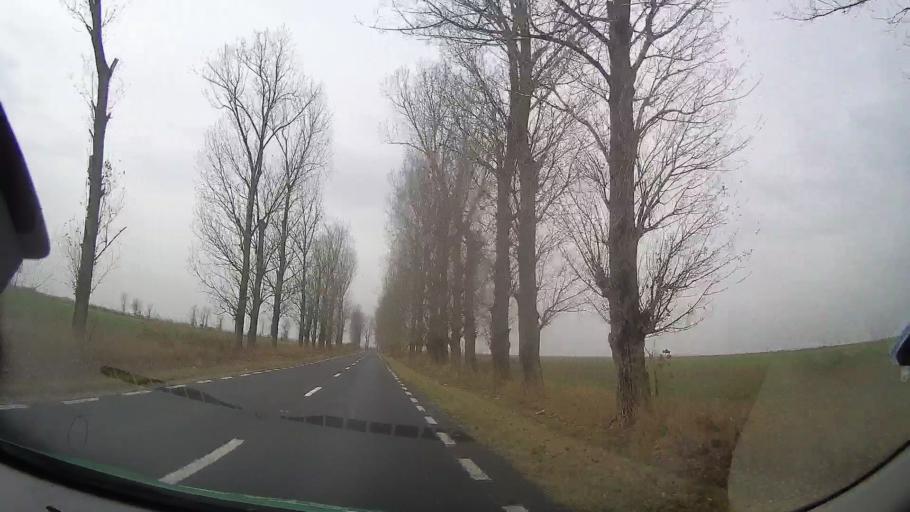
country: RO
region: Ilfov
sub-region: Comuna Gruiu
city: Lipia
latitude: 44.7231
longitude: 26.2766
